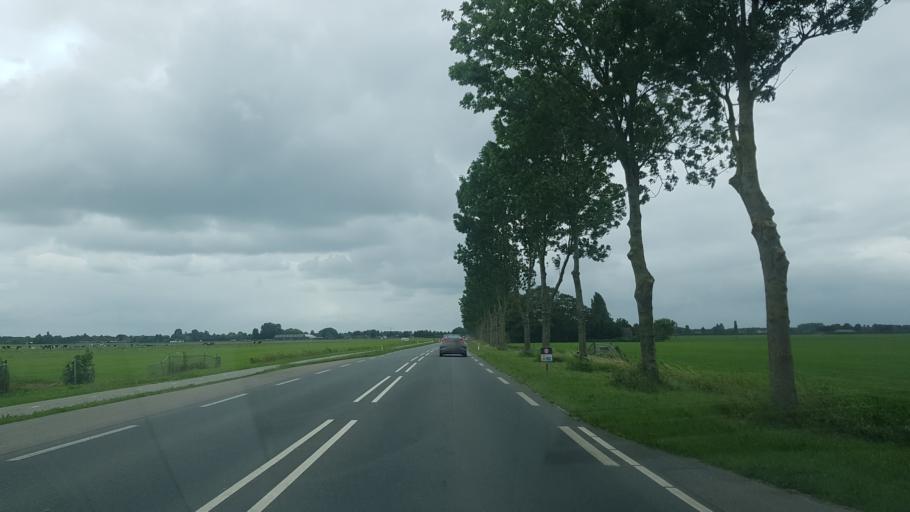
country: NL
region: North Holland
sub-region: Gemeente Hoorn
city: Hoorn
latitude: 52.6549
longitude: 5.1373
